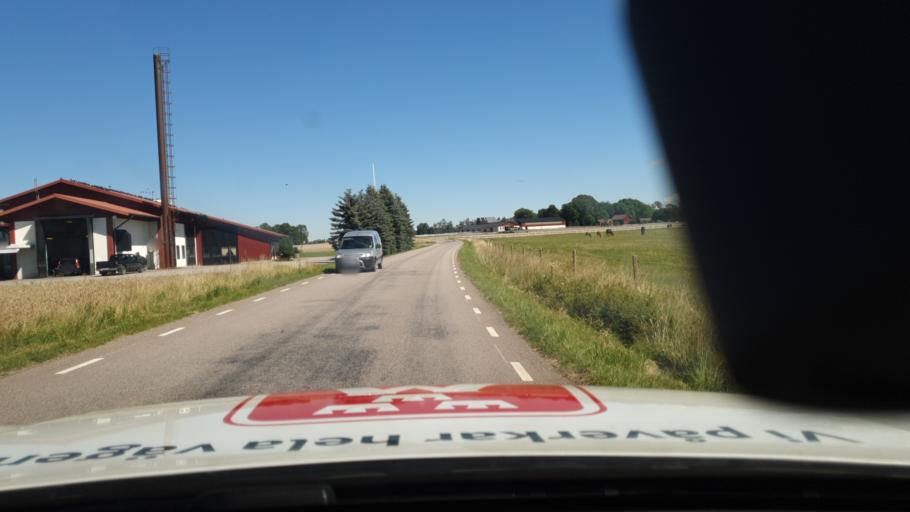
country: SE
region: Vaestra Goetaland
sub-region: Lidkopings Kommun
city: Vinninga
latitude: 58.4371
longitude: 13.2154
